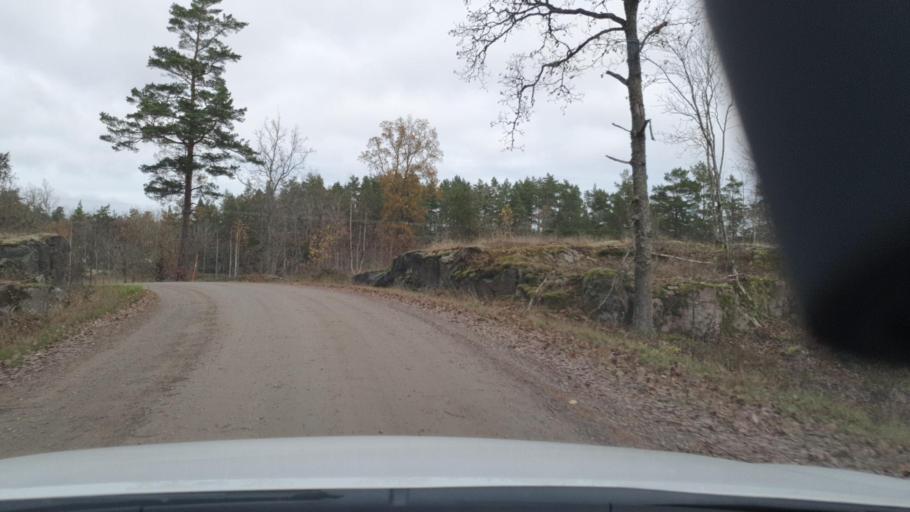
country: SE
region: Kalmar
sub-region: Vasterviks Kommun
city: Vaestervik
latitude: 57.7262
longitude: 16.4798
